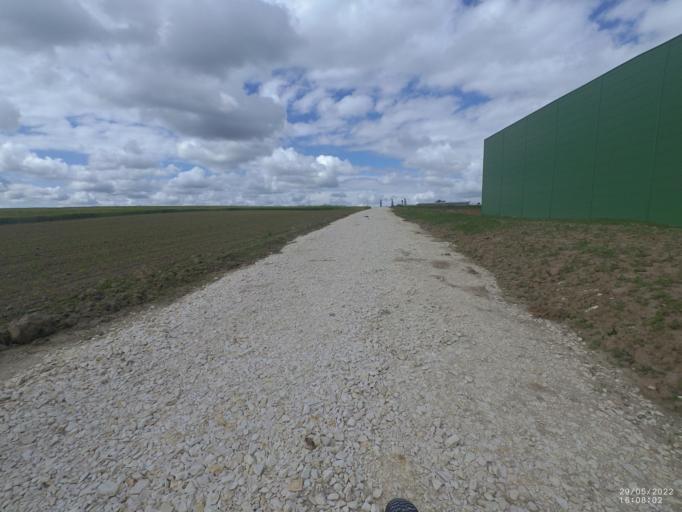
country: DE
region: Baden-Wuerttemberg
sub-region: Regierungsbezirk Stuttgart
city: Bolheim
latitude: 48.5899
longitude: 10.1206
